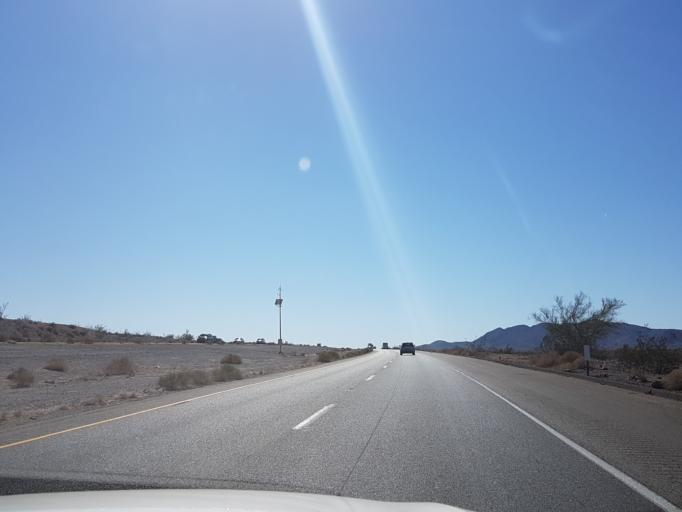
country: US
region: California
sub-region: San Bernardino County
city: Fort Irwin
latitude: 35.1869
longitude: -116.1626
